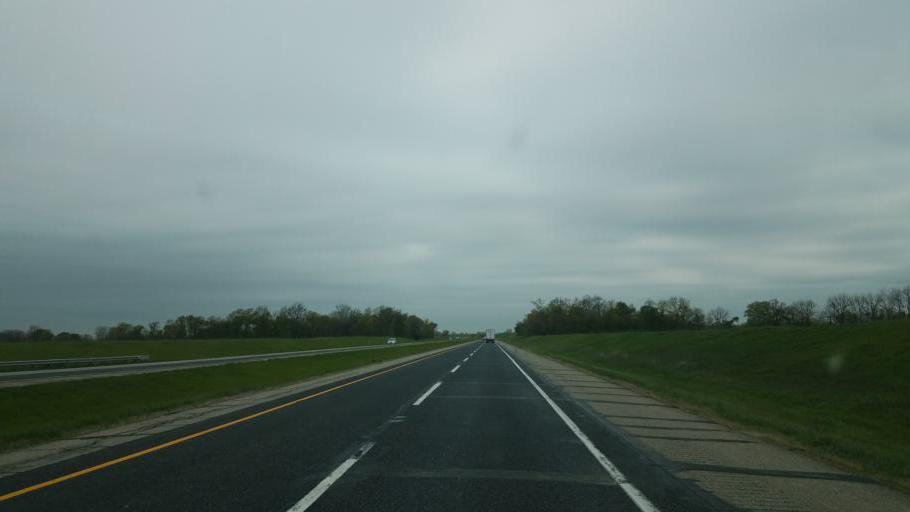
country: US
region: Michigan
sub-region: Saint Joseph County
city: Sturgis
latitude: 41.7493
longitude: -85.3799
